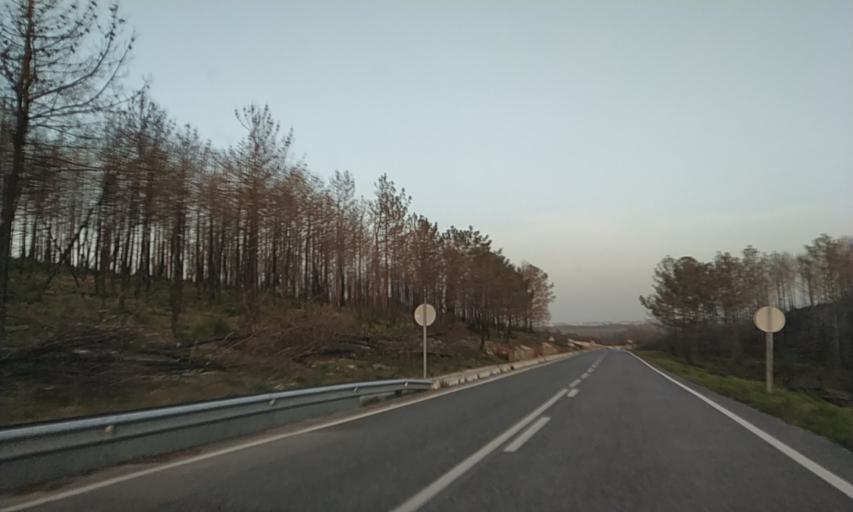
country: PT
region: Leiria
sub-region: Marinha Grande
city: Marinha Grande
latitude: 39.7462
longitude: -8.9923
